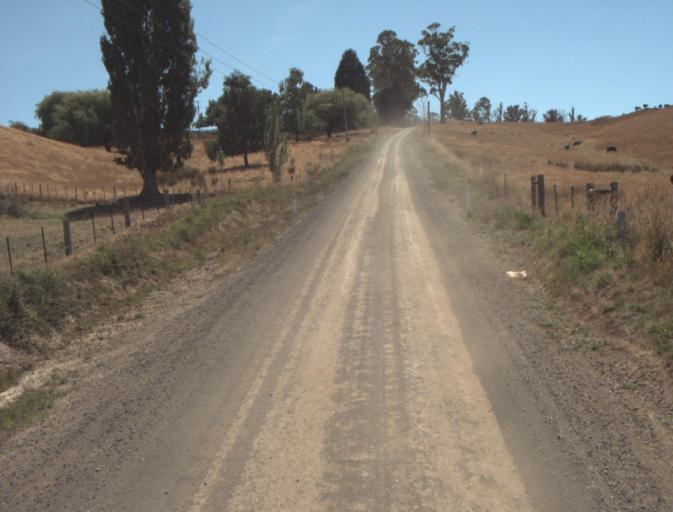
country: AU
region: Tasmania
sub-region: Launceston
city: Mayfield
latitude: -41.2513
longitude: 147.1340
